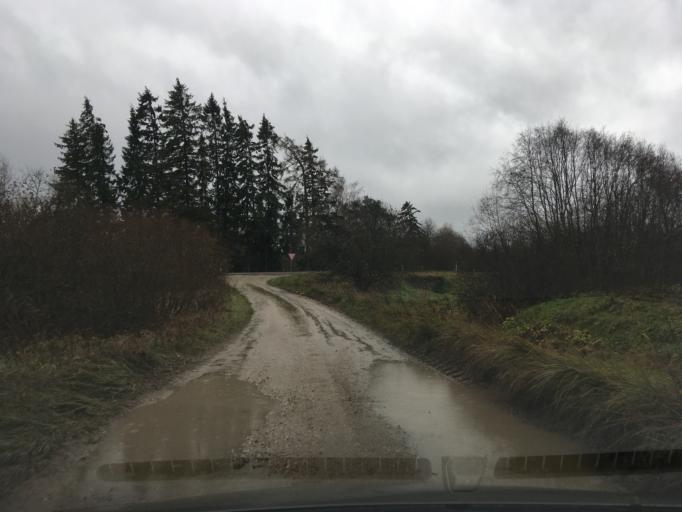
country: EE
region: Laeaene
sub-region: Lihula vald
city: Lihula
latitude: 58.7009
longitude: 23.8564
